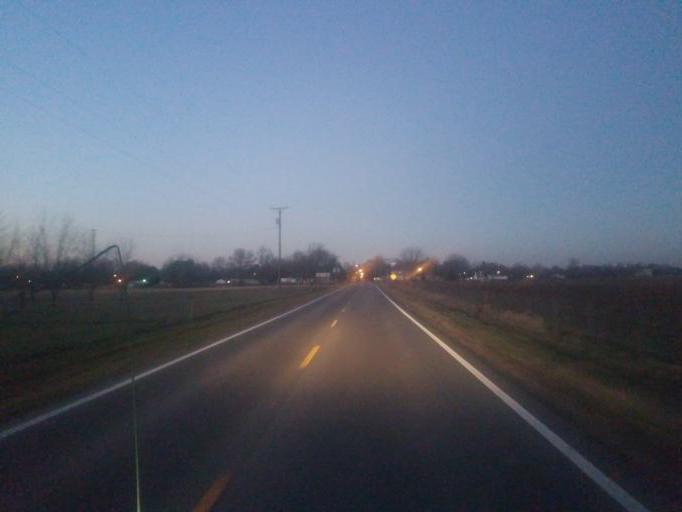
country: US
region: Ohio
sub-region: Wyandot County
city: Upper Sandusky
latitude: 40.8086
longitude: -83.1308
